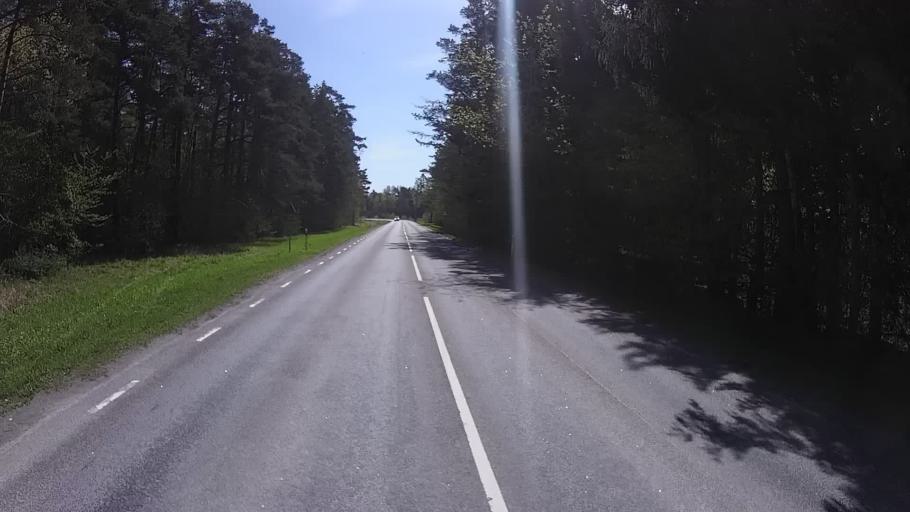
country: EE
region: Laeaene
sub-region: Haapsalu linn
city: Haapsalu
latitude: 58.9077
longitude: 23.5628
